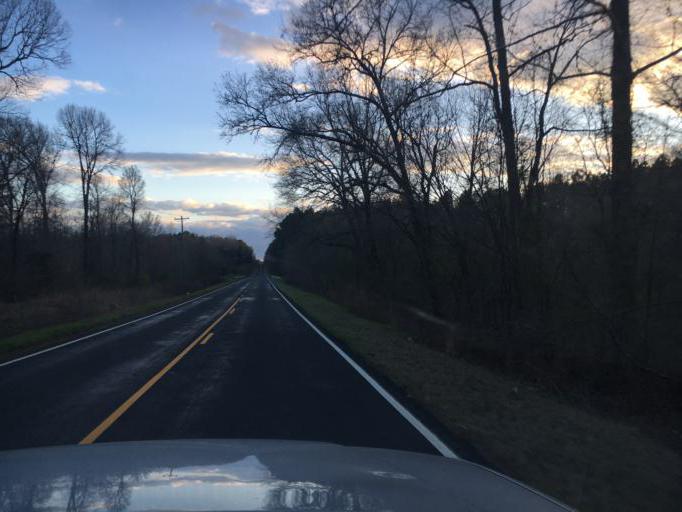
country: US
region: South Carolina
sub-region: Greenwood County
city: Greenwood
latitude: 34.0761
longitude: -82.2202
